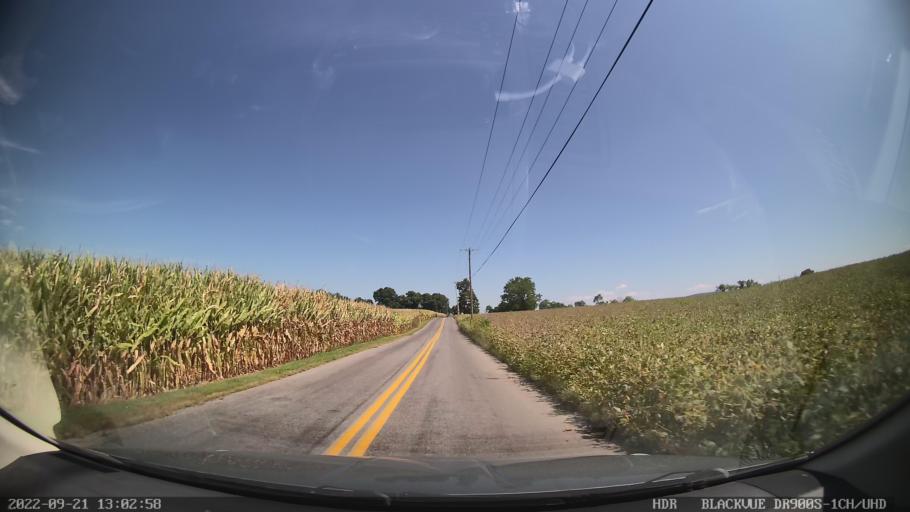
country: US
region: Pennsylvania
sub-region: Berks County
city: Kutztown
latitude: 40.4962
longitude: -75.7595
